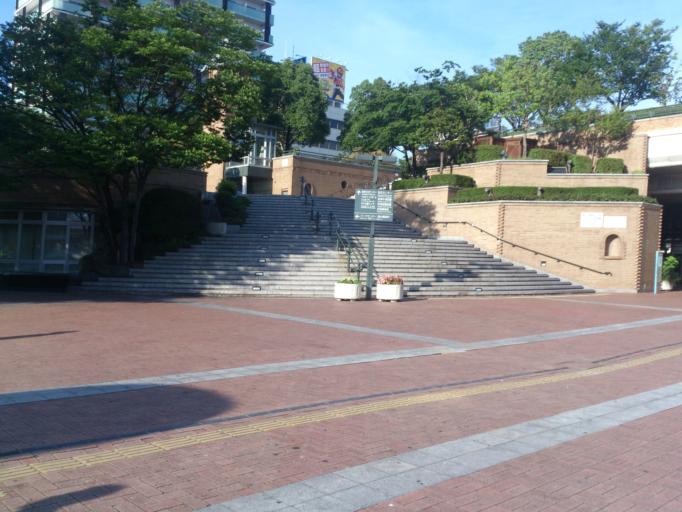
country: JP
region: Hyogo
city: Amagasaki
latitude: 34.7191
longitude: 135.4170
